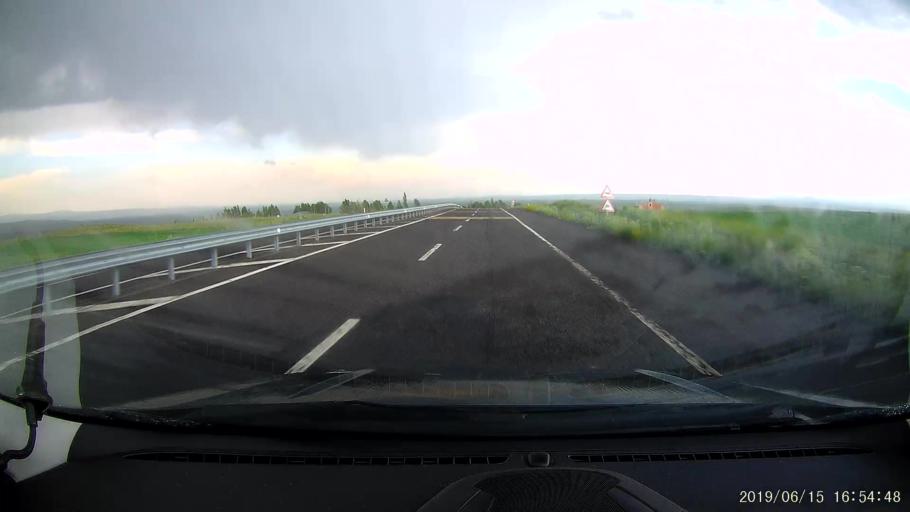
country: TR
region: Kars
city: Susuz
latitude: 40.7885
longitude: 43.1322
